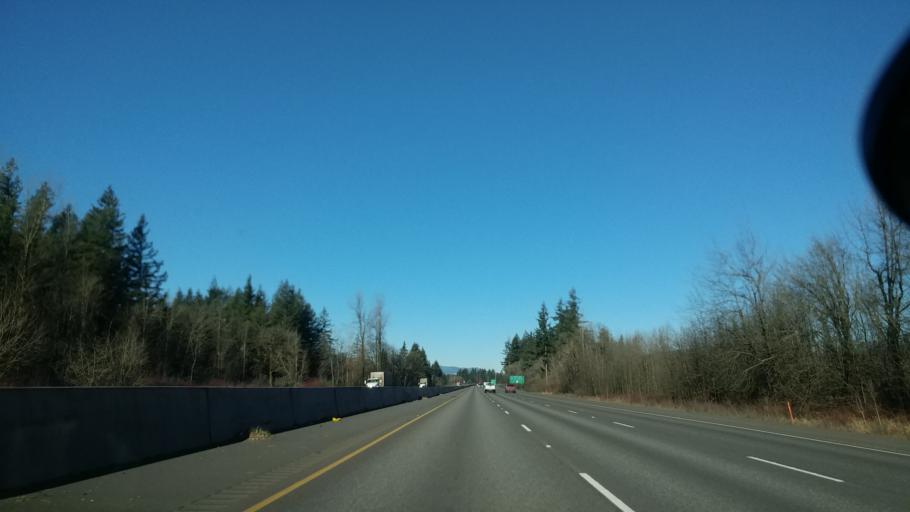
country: US
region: Washington
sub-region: Thurston County
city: Grand Mound
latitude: 46.7866
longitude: -123.0058
